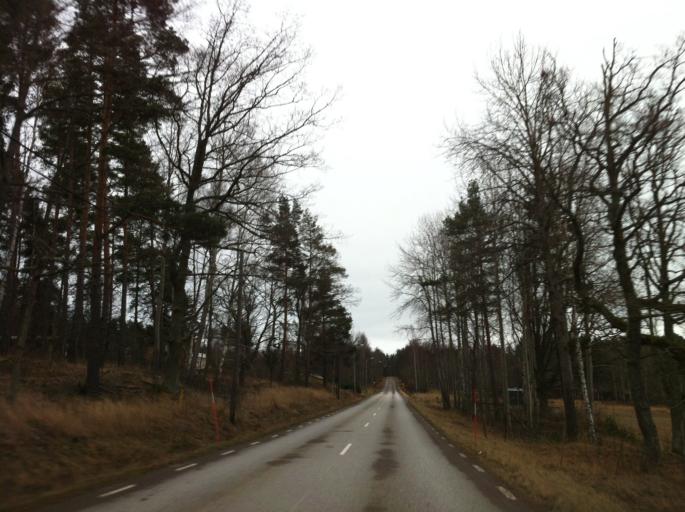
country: SE
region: Kalmar
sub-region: Vasterviks Kommun
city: Vaestervik
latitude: 57.8088
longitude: 16.5909
